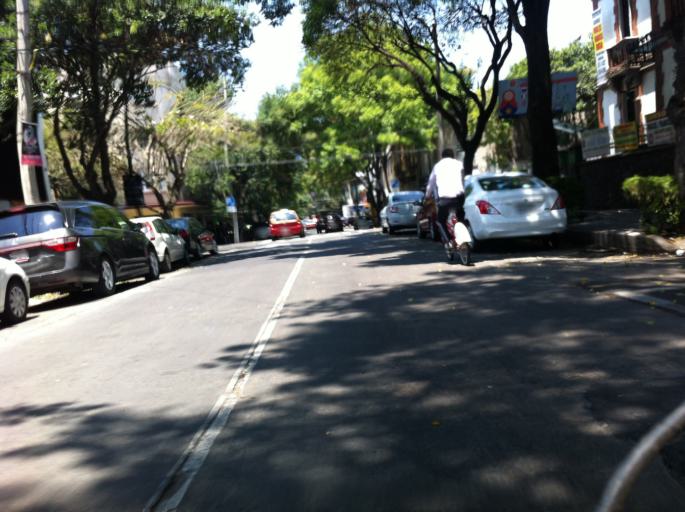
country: MX
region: Mexico City
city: Benito Juarez
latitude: 19.4190
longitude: -99.1575
